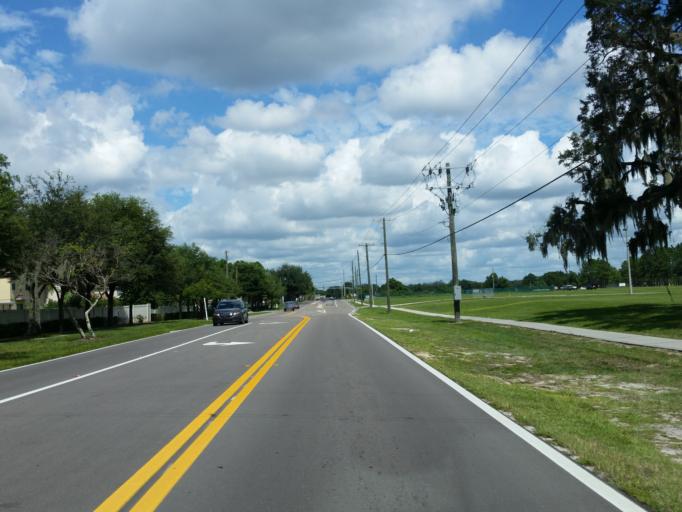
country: US
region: Florida
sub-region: Hillsborough County
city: Riverview
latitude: 27.8500
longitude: -82.3145
